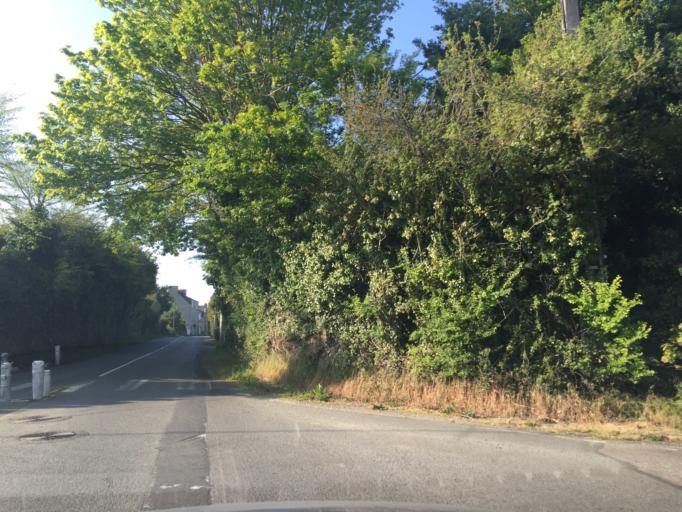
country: FR
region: Brittany
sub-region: Departement des Cotes-d'Armor
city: Saint-Cast-le-Guildo
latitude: 48.6135
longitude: -2.2537
